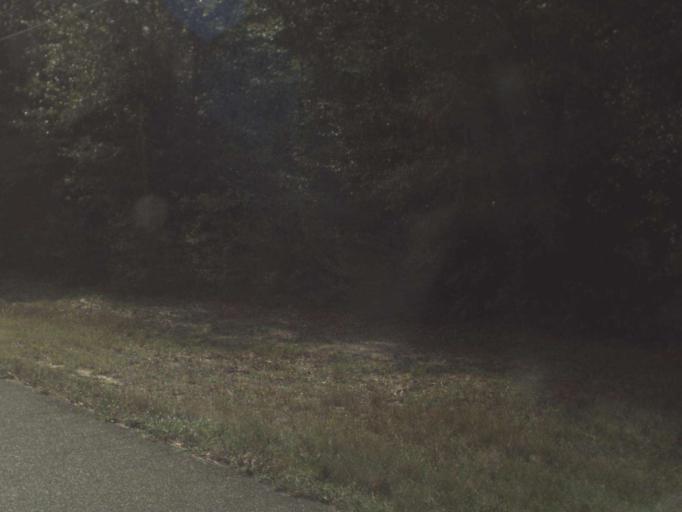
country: US
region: Florida
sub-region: Santa Rosa County
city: Point Baker
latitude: 30.7223
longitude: -87.0448
